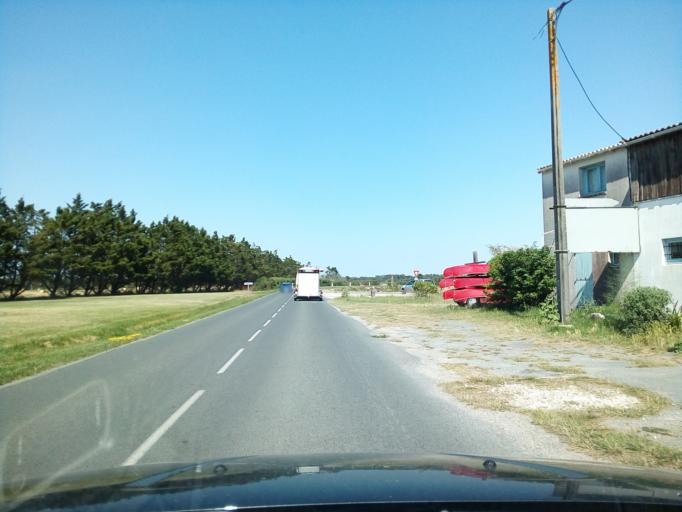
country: FR
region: Poitou-Charentes
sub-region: Departement de la Charente-Maritime
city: Boyard-Ville
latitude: 45.9673
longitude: -1.2676
